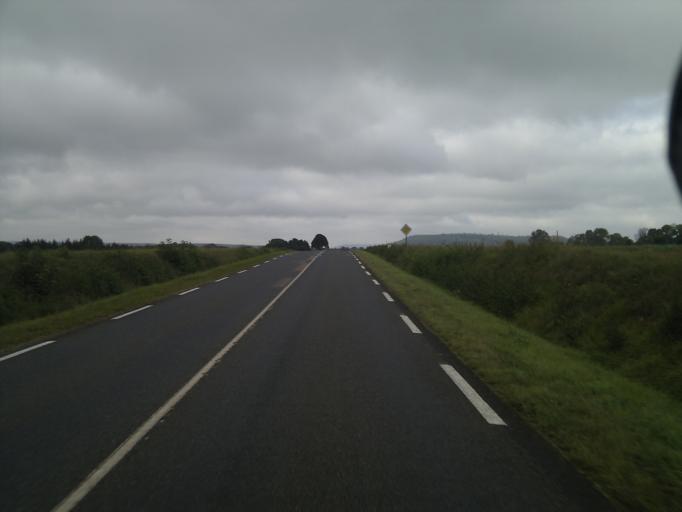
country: FR
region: Lorraine
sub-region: Departement des Vosges
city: Liffol-le-Grand
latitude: 48.2729
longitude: 5.4299
